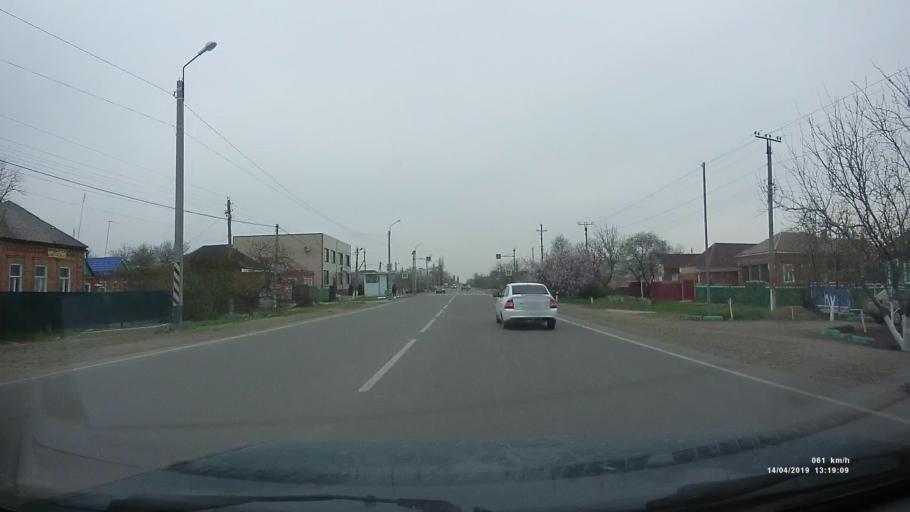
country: RU
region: Rostov
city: Kuleshovka
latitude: 47.0799
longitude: 39.5489
